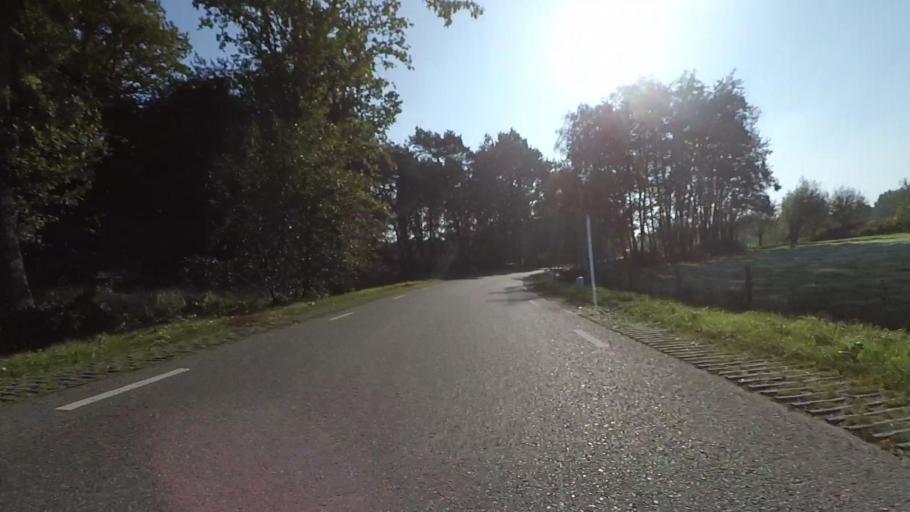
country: NL
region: Gelderland
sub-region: Gemeente Putten
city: Putten
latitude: 52.2448
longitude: 5.5529
